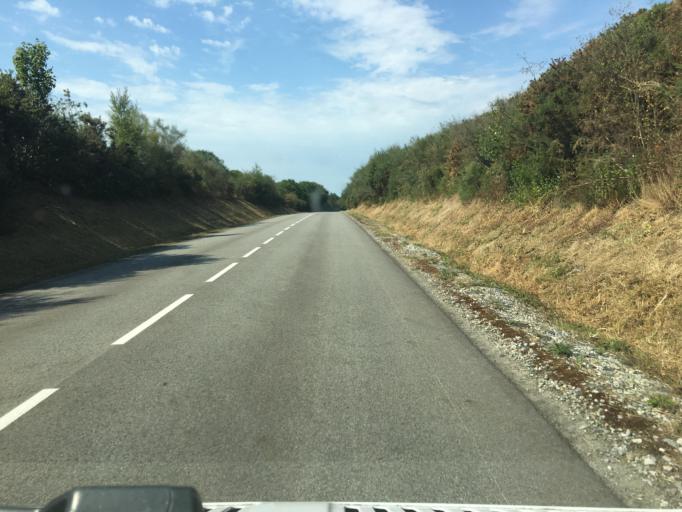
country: FR
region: Brittany
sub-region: Departement des Cotes-d'Armor
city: Mur-de-Bretagne
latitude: 48.2184
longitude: -3.0592
